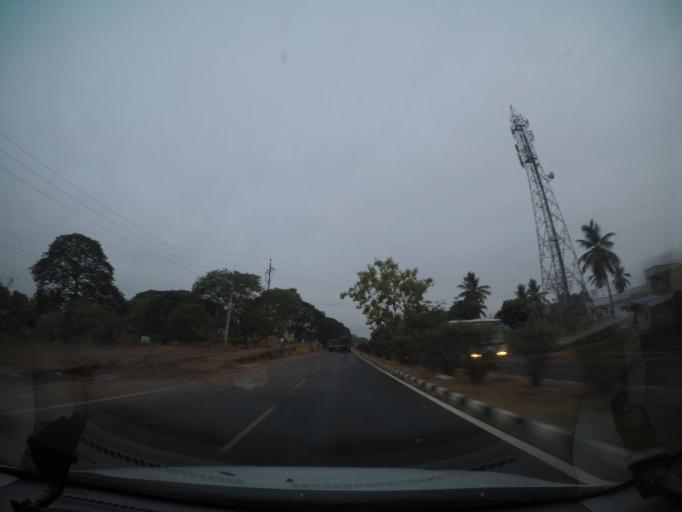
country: IN
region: Andhra Pradesh
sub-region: West Godavari
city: Eluru
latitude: 16.8047
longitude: 81.3032
